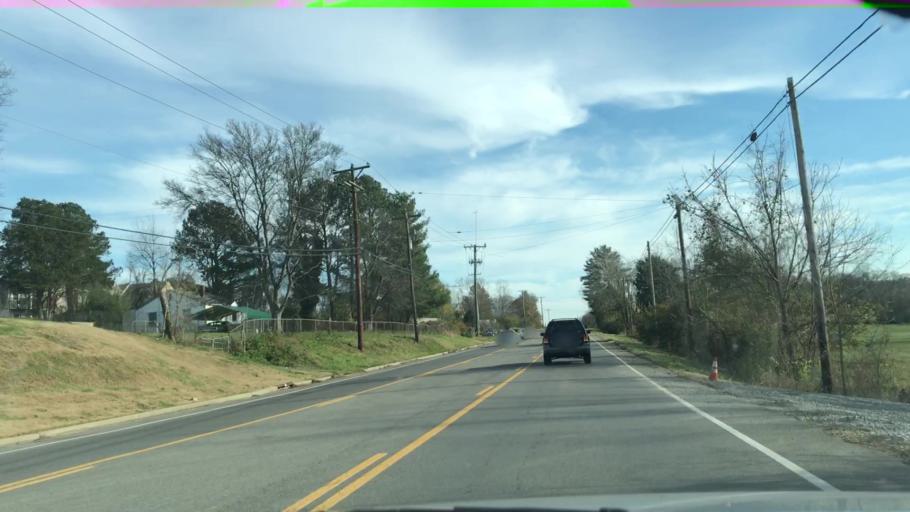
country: US
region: Tennessee
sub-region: Williamson County
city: Nolensville
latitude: 36.0027
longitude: -86.6971
